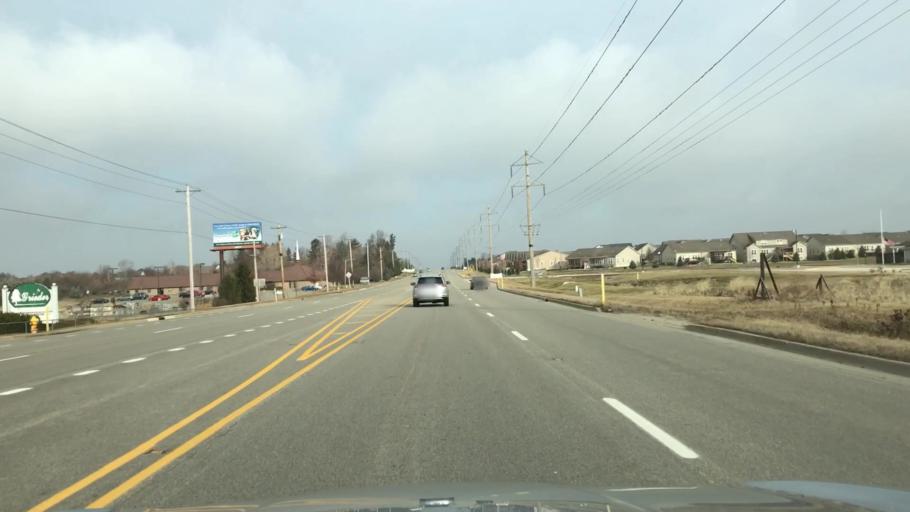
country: US
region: Illinois
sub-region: McLean County
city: Normal
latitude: 40.5034
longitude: -88.9027
